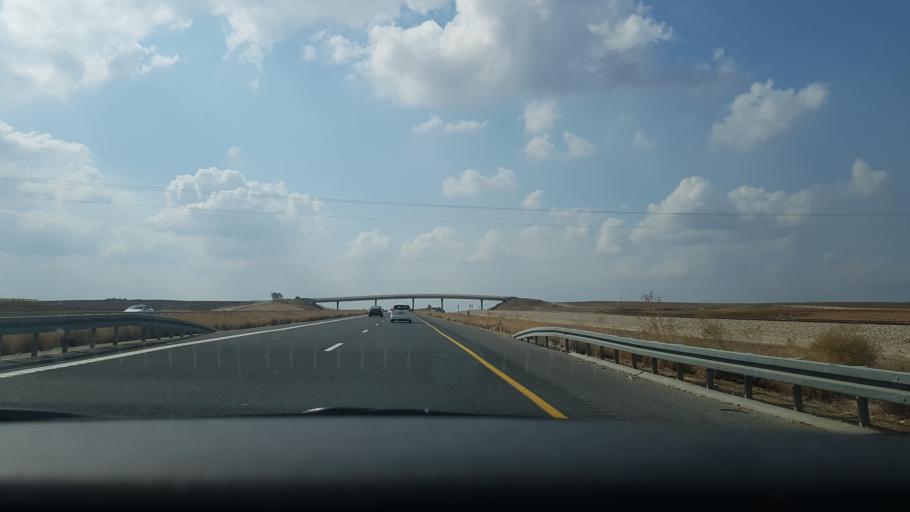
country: IL
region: Central District
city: Gedera
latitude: 31.7671
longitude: 34.8289
